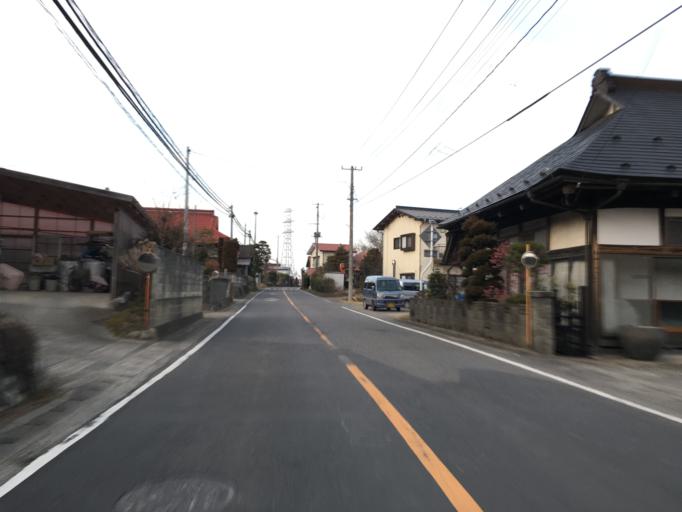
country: JP
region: Ibaraki
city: Daigo
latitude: 36.9213
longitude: 140.4078
